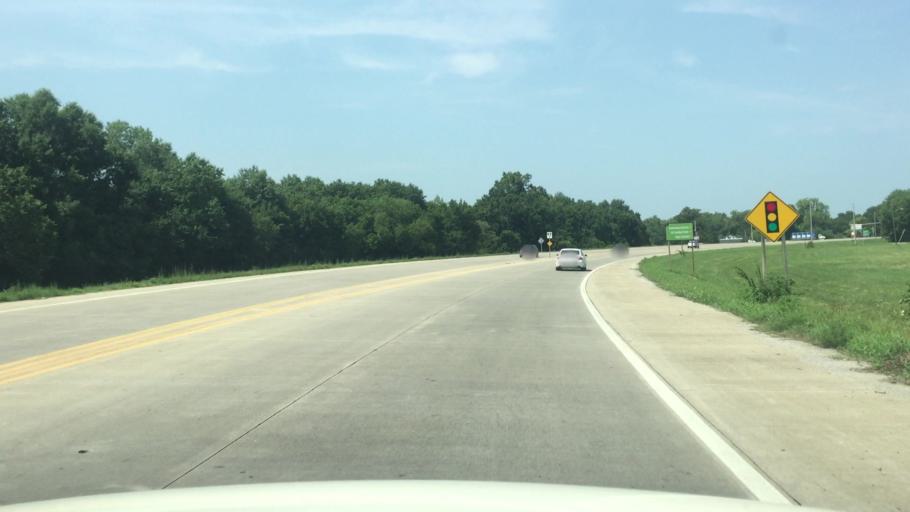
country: US
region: Kansas
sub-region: Crawford County
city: Pittsburg
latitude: 37.4073
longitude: -94.7246
